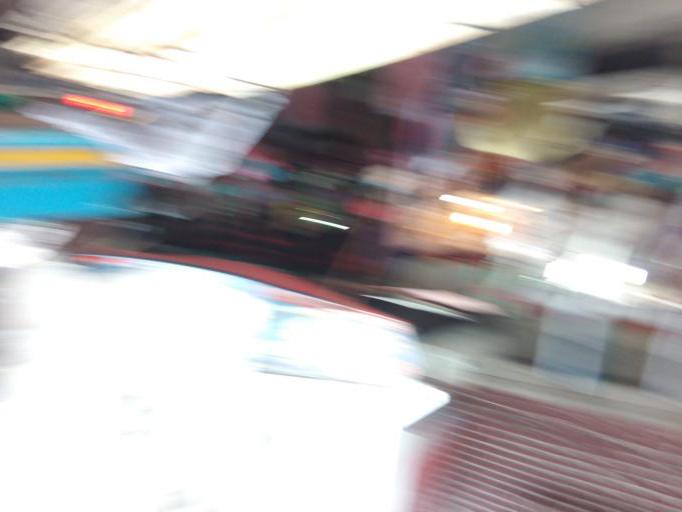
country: BD
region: Dhaka
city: Azimpur
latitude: 23.7205
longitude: 90.3740
